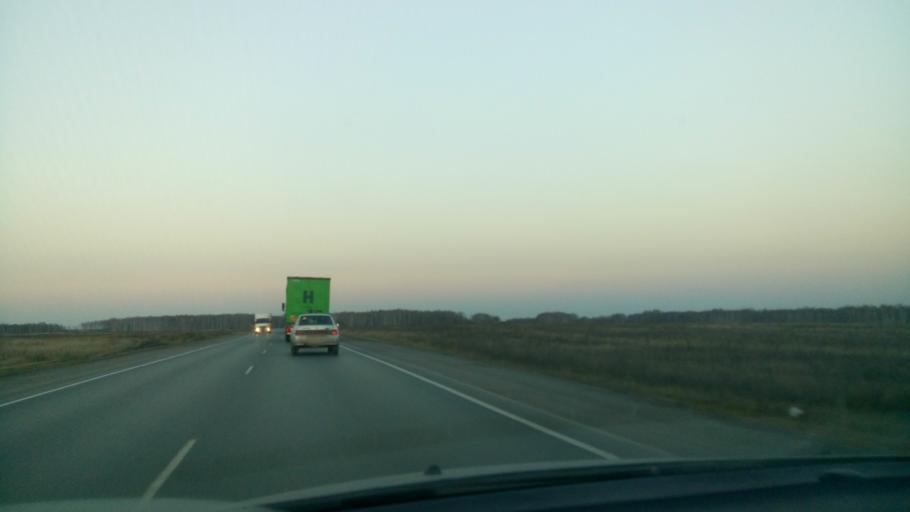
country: RU
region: Sverdlovsk
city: Pyshma
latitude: 56.9223
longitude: 63.1420
